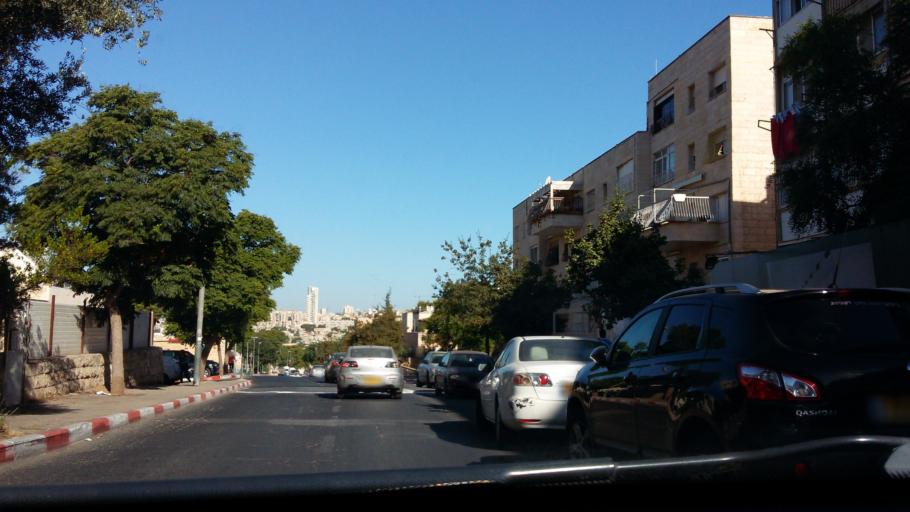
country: IL
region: Jerusalem
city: Jerusalem
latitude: 31.7550
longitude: 35.2167
